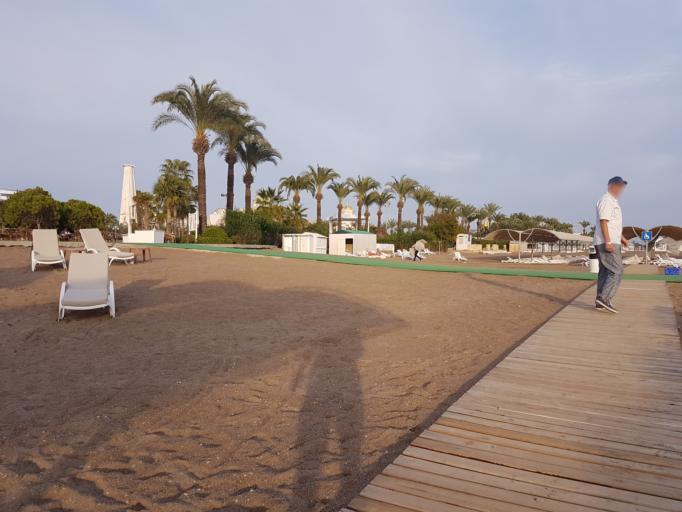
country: TR
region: Antalya
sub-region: Serik
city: Kumkoey
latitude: 36.8519
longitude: 30.8601
